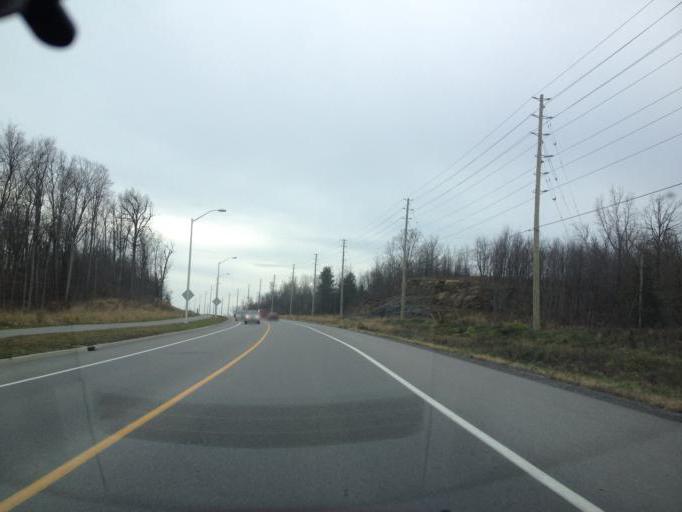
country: CA
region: Ontario
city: Bells Corners
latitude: 45.3302
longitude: -75.9503
